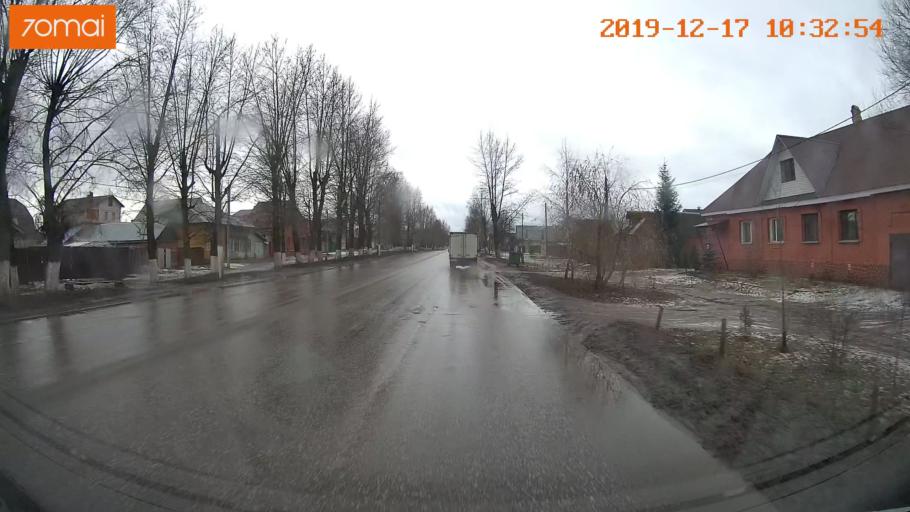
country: RU
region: Vladimir
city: Gus'-Khrustal'nyy
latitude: 55.6260
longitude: 40.6852
